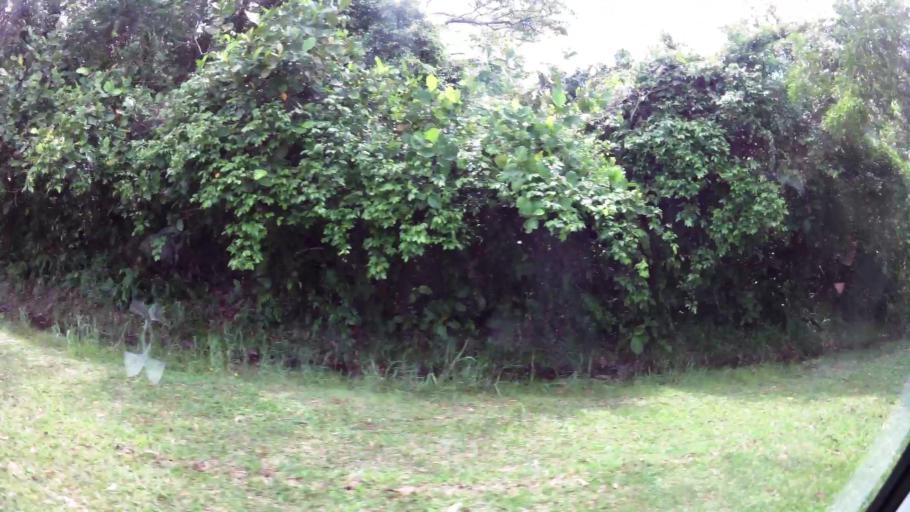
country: BN
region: Belait
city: Seria
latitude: 4.5986
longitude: 114.2909
